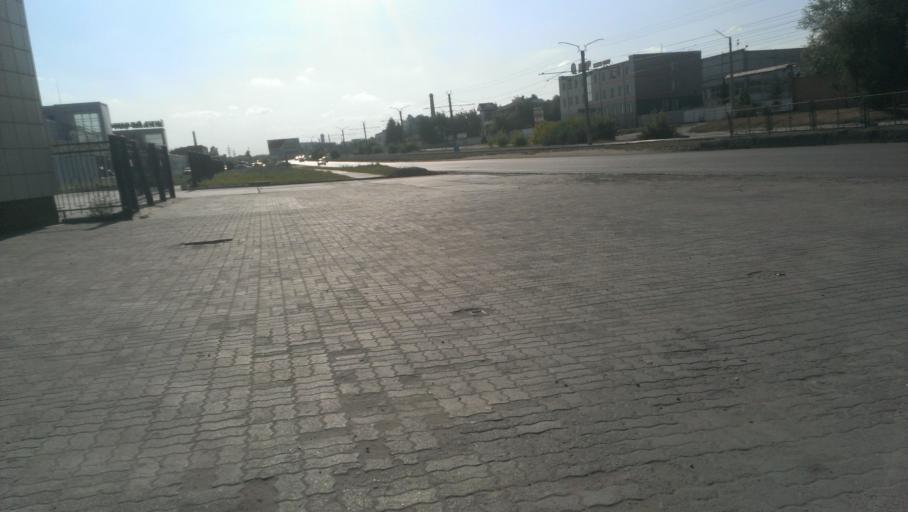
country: RU
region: Altai Krai
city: Novosilikatnyy
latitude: 53.3231
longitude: 83.6422
